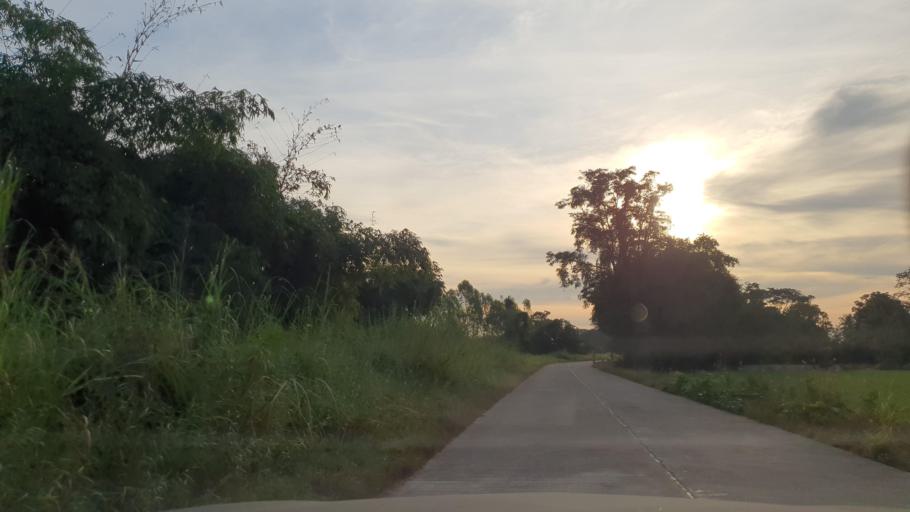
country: TH
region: Nakhon Sawan
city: Krok Phra
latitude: 15.6623
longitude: 100.0162
